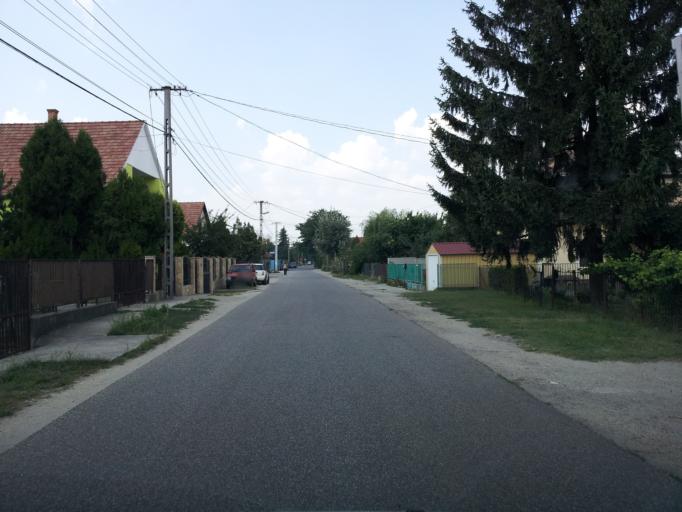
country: HU
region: Pest
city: Szigethalom
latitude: 47.3201
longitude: 19.0147
